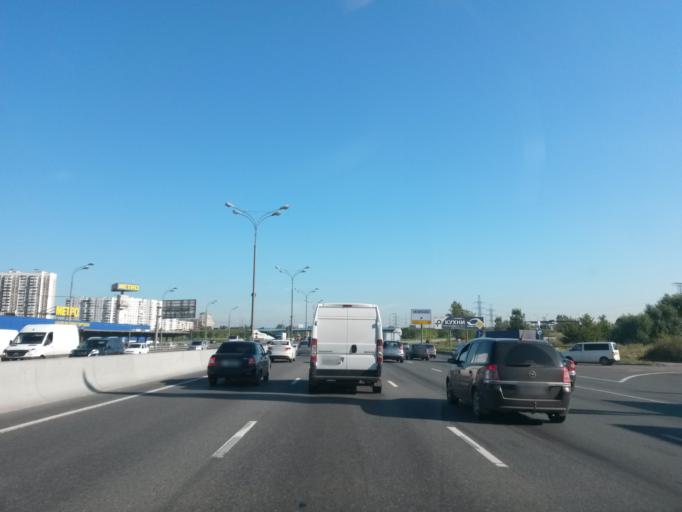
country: RU
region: Moscow
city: Vostochnyy
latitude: 55.8099
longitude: 37.8394
